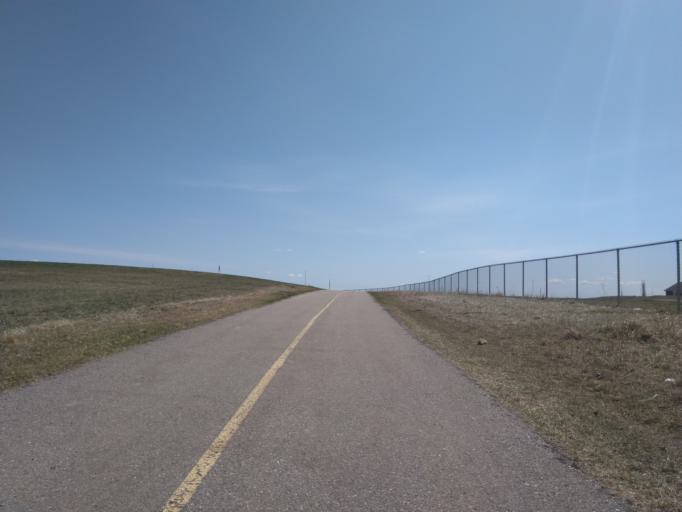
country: CA
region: Alberta
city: Chestermere
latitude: 51.1110
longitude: -113.9259
